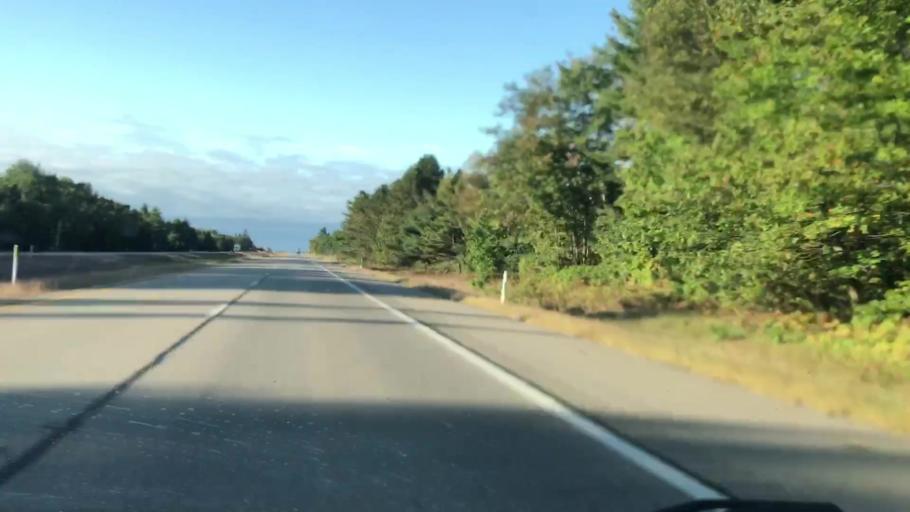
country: US
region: Michigan
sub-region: Chippewa County
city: Sault Ste. Marie
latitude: 46.4332
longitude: -84.3898
